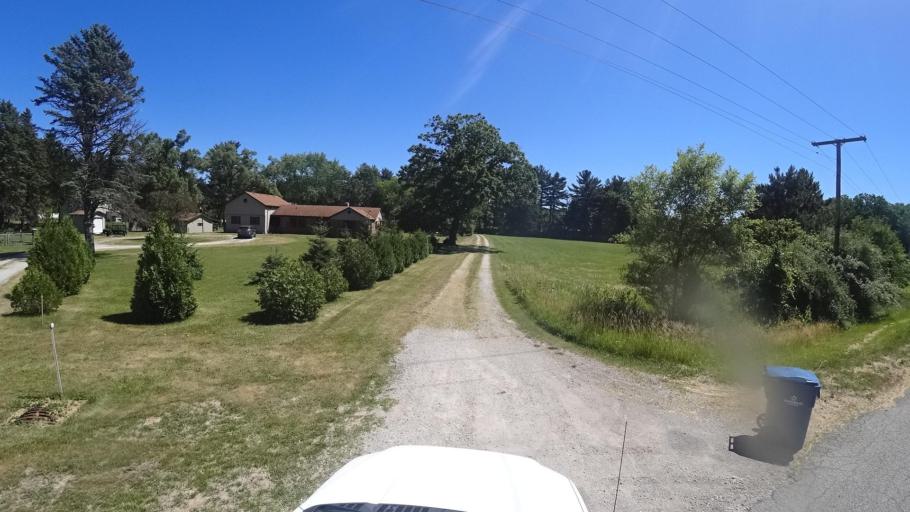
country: US
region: Indiana
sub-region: Porter County
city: Porter
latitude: 41.6259
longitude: -87.0819
